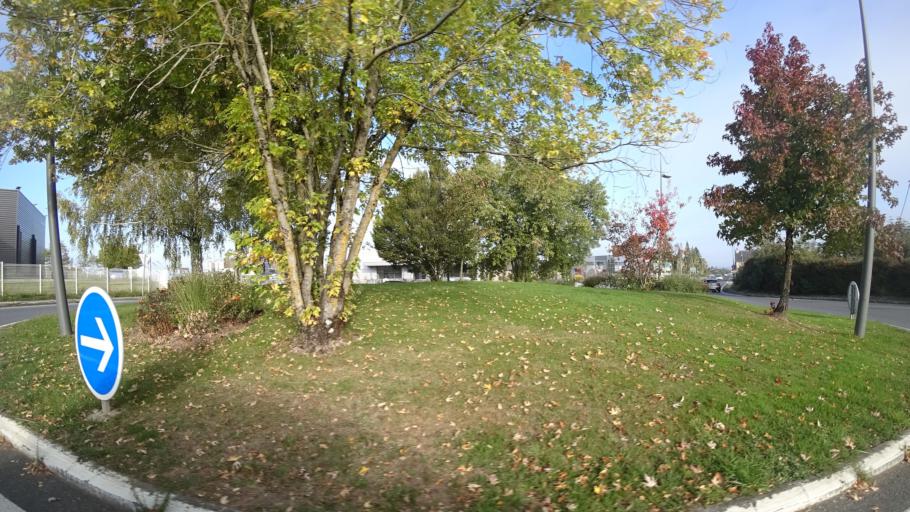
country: FR
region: Midi-Pyrenees
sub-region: Departement de l'Aveyron
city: Luc-la-Primaube
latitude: 44.3008
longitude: 2.5568
